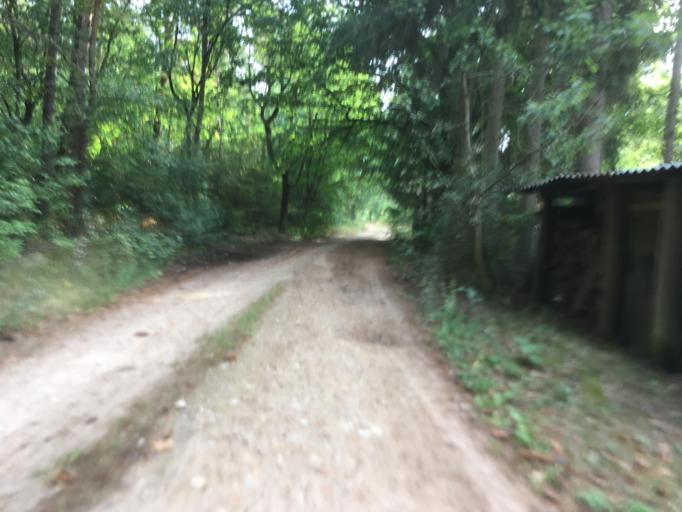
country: DE
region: Brandenburg
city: Templin
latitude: 52.9954
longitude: 13.5385
